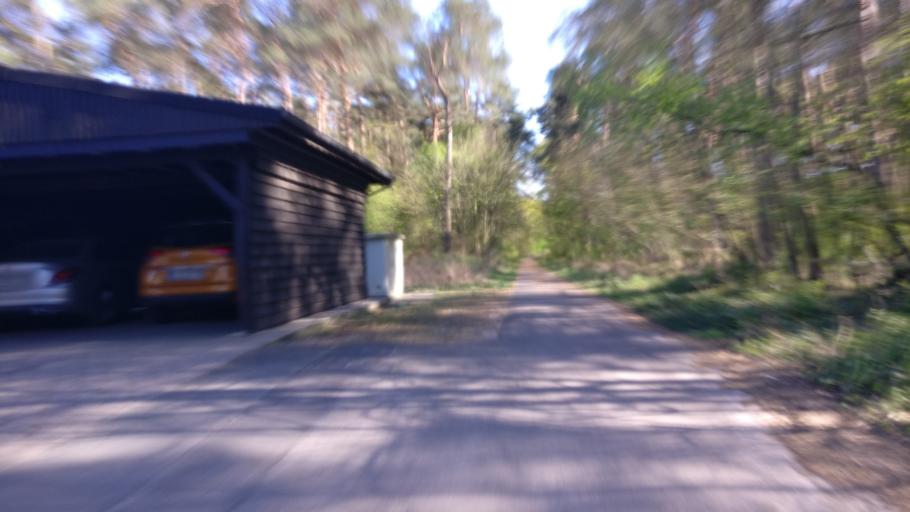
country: DE
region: North Rhine-Westphalia
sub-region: Regierungsbezirk Detmold
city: Lage
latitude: 52.0122
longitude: 8.7664
